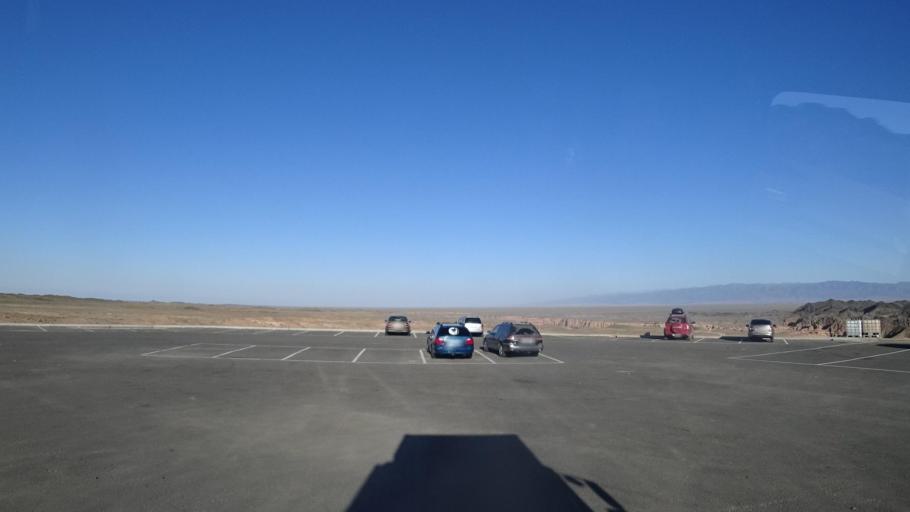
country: KZ
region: Almaty Oblysy
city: Kegen
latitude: 43.3563
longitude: 79.0544
